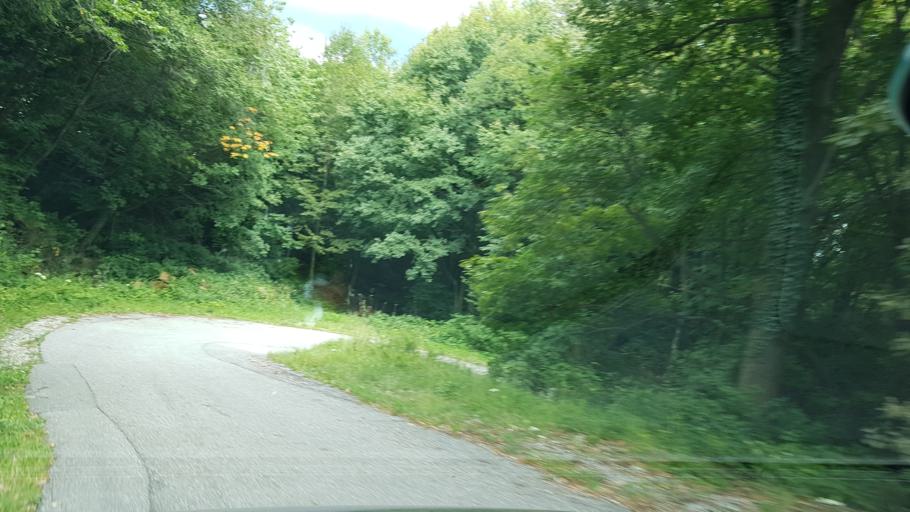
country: SI
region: Kanal
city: Deskle
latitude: 46.0683
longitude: 13.5737
